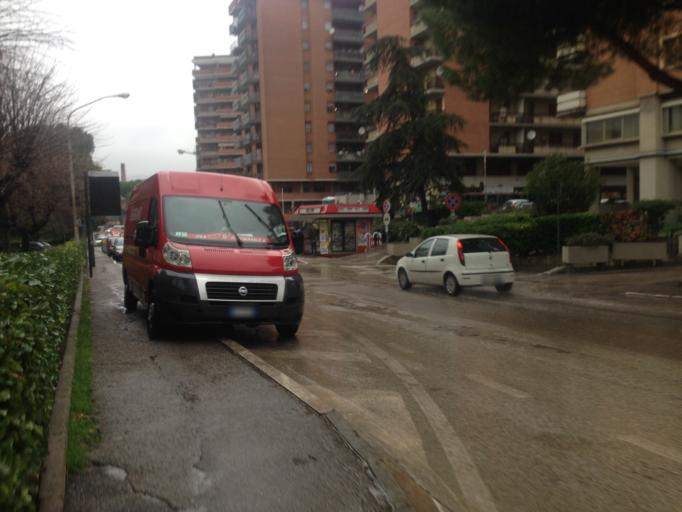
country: IT
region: Umbria
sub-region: Provincia di Perugia
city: Perugia
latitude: 43.1056
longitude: 12.3685
